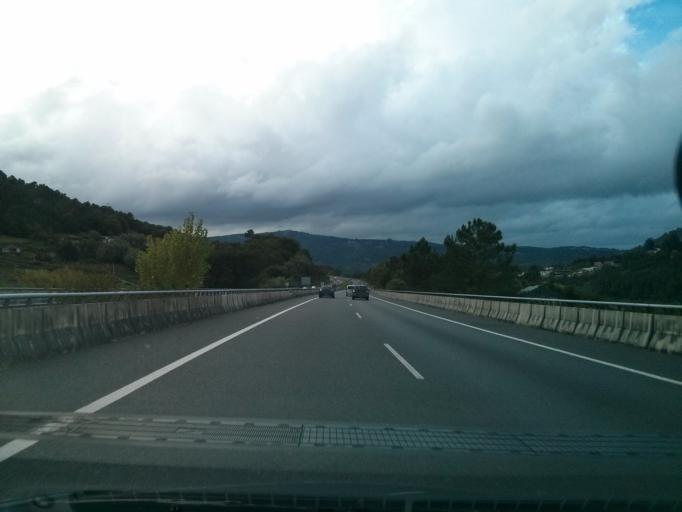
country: ES
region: Galicia
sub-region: Provincia de Ourense
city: Toen
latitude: 42.3318
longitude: -7.9615
